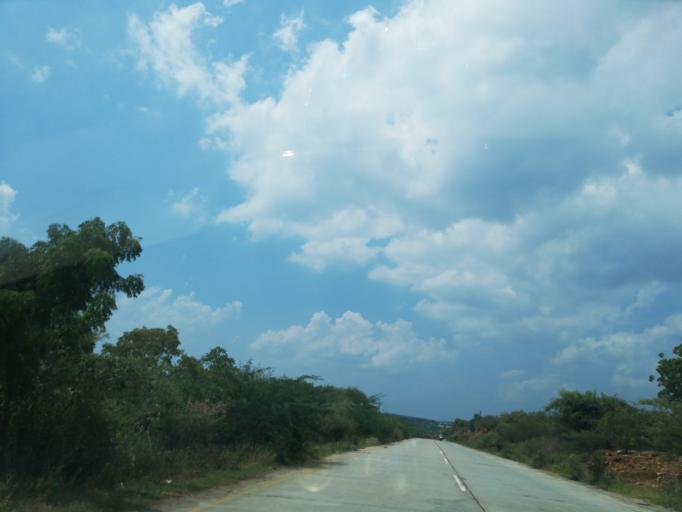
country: IN
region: Andhra Pradesh
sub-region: Guntur
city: Macherla
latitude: 16.5694
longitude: 79.3329
